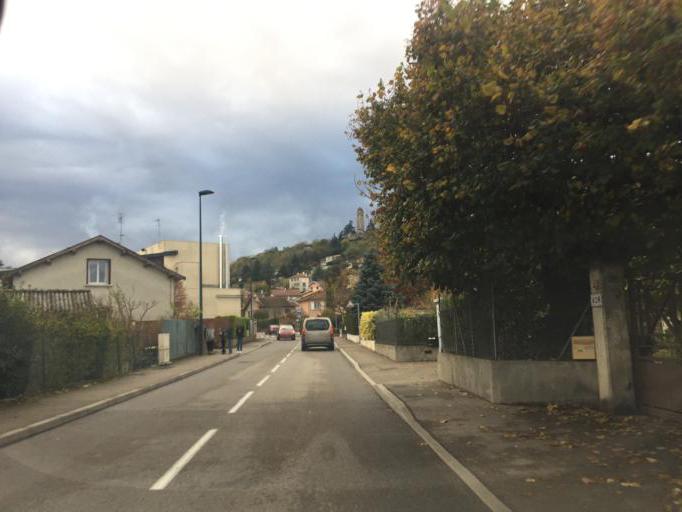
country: FR
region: Rhone-Alpes
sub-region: Departement de l'Ain
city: Miribel
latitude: 45.8274
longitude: 4.9584
